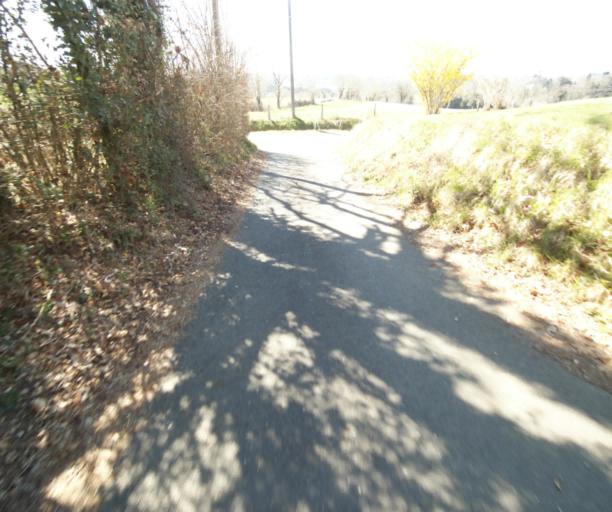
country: FR
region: Limousin
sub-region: Departement de la Correze
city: Chamboulive
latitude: 45.4338
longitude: 1.7155
